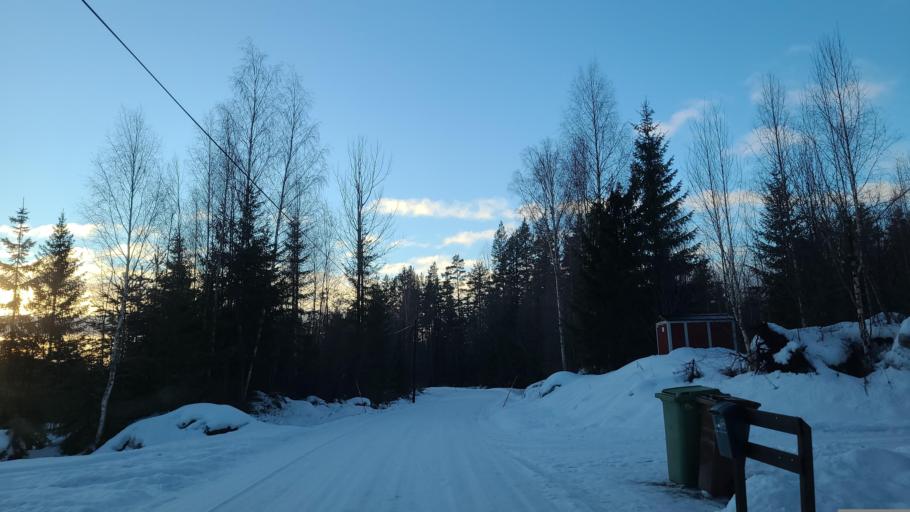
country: SE
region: Gaevleborg
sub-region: Bollnas Kommun
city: Kilafors
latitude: 61.3738
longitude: 16.6810
